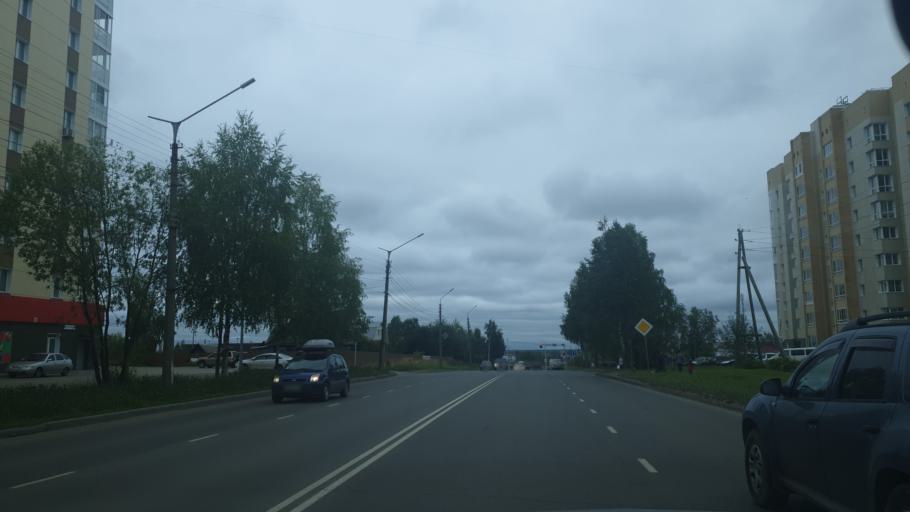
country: RU
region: Komi Republic
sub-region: Syktyvdinskiy Rayon
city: Syktyvkar
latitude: 61.6408
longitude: 50.8117
